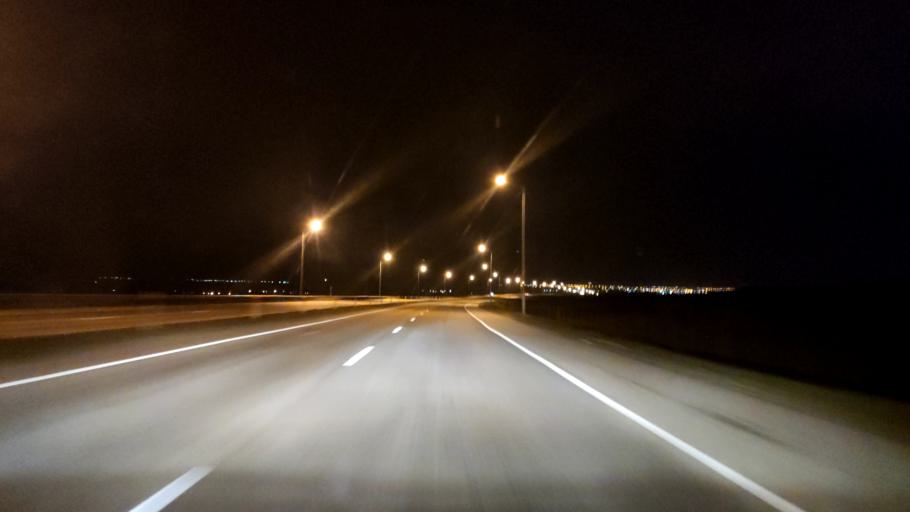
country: RU
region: Belgorod
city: Staryy Oskol
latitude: 51.3375
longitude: 37.7687
